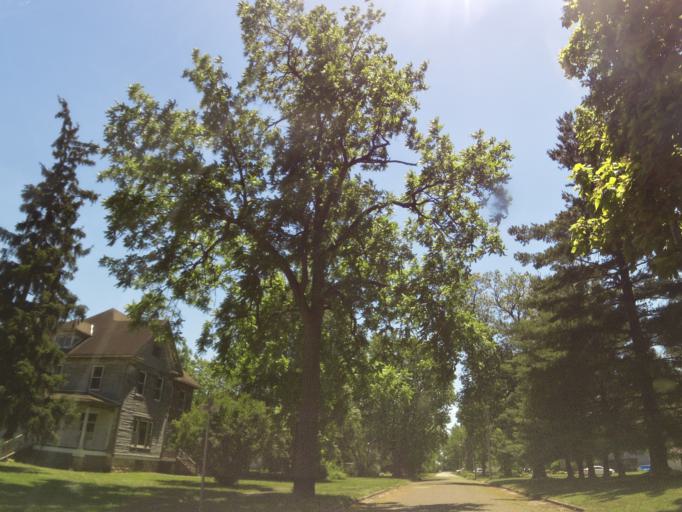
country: US
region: Illinois
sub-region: Livingston County
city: Chatsworth
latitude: 40.7563
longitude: -88.1849
